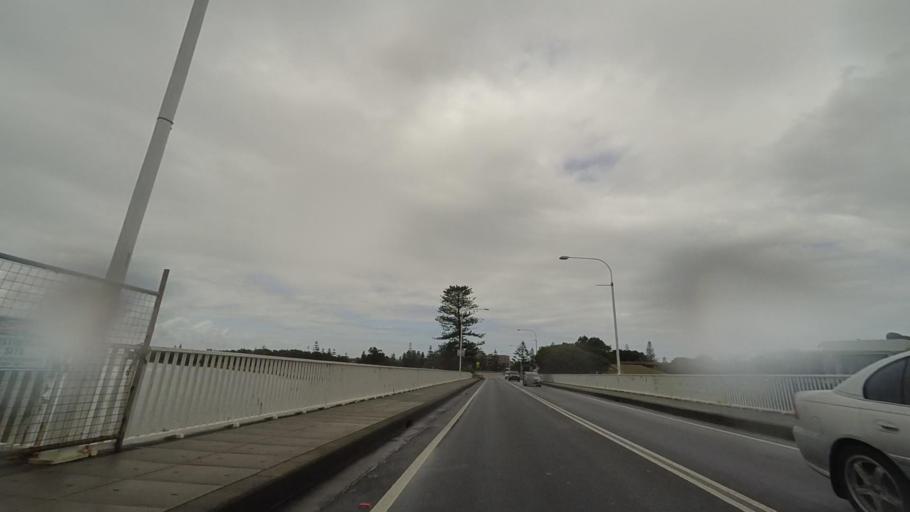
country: AU
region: New South Wales
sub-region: Wyong Shire
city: The Entrance
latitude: -33.3367
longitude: 151.5013
